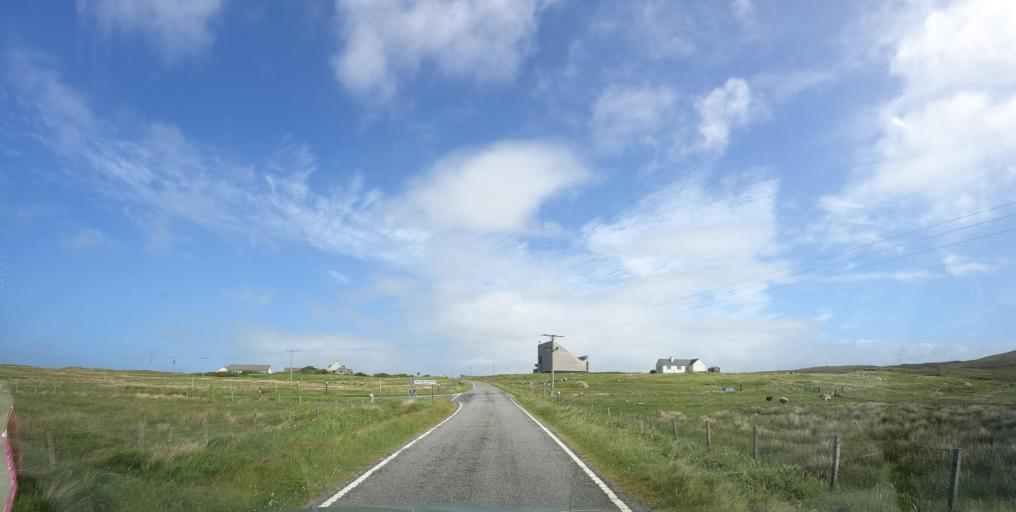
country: GB
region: Scotland
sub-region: Eilean Siar
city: Isle of South Uist
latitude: 57.1231
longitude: -7.3603
